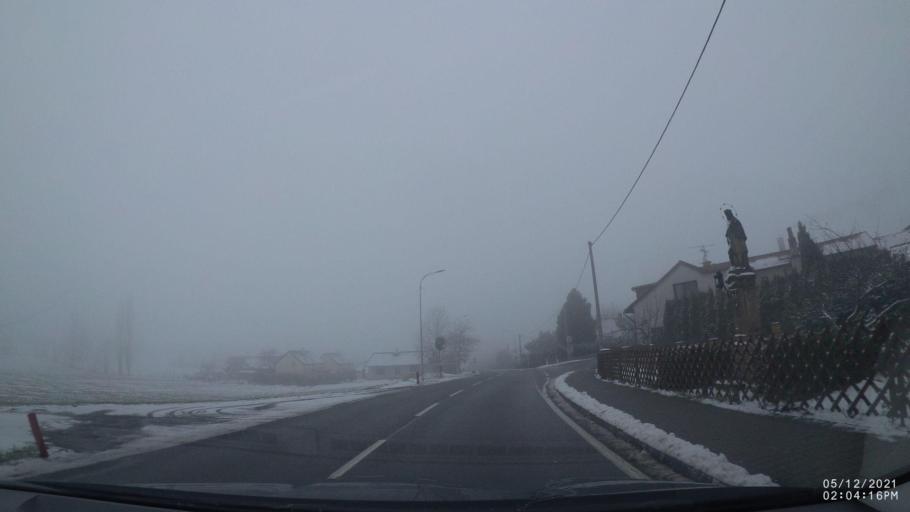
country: CZ
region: Kralovehradecky
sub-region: Okres Nachod
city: Cerveny Kostelec
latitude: 50.4921
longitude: 16.1227
